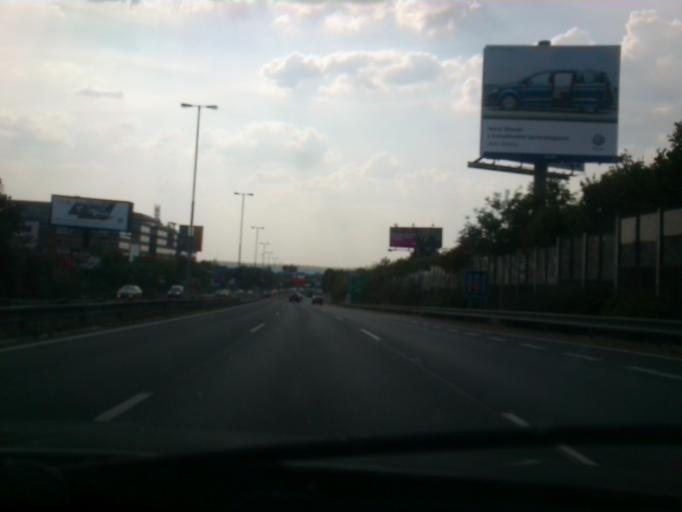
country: CZ
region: Praha
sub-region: Praha 8
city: Karlin
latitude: 50.0403
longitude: 14.4799
